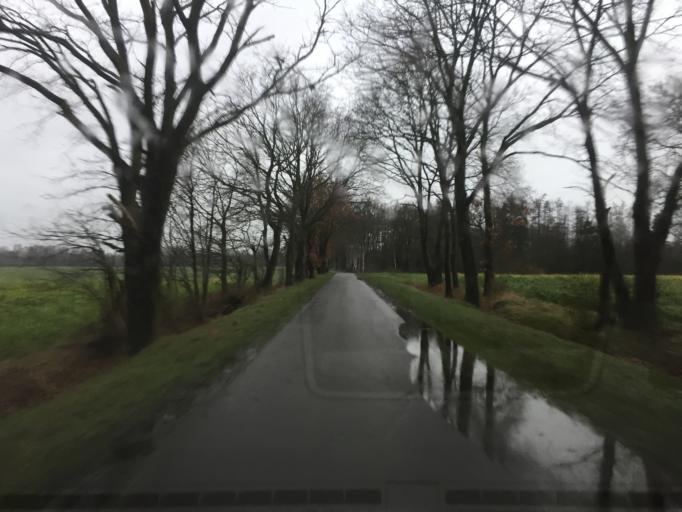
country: DE
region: Lower Saxony
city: Borstel
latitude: 52.6395
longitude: 8.9256
